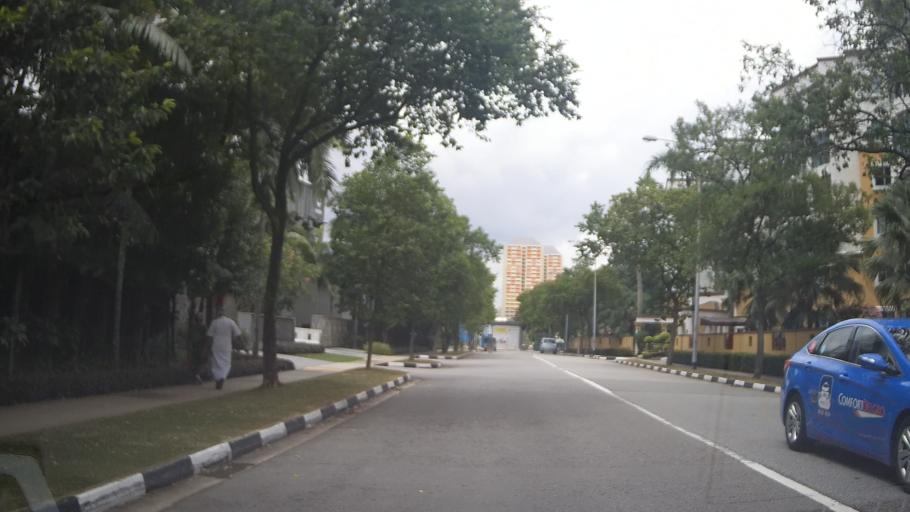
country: SG
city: Singapore
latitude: 1.2982
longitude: 103.7655
